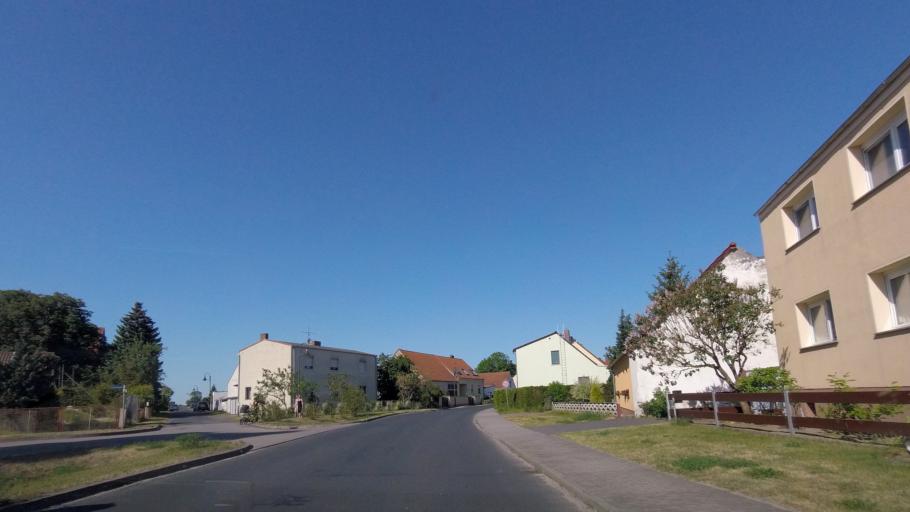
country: DE
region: Brandenburg
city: Brandenburg an der Havel
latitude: 52.3720
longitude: 12.6356
